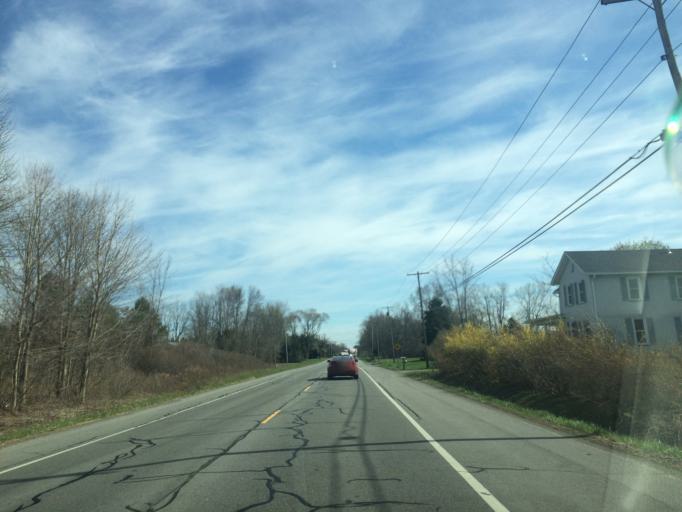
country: US
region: New York
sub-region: Monroe County
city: Webster
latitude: 43.1948
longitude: -77.4304
